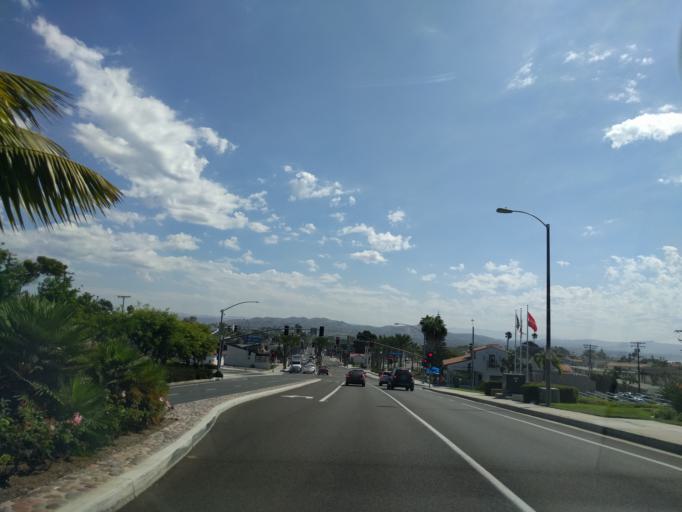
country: US
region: California
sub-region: Orange County
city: Dana Point
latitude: 33.4654
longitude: -117.7076
